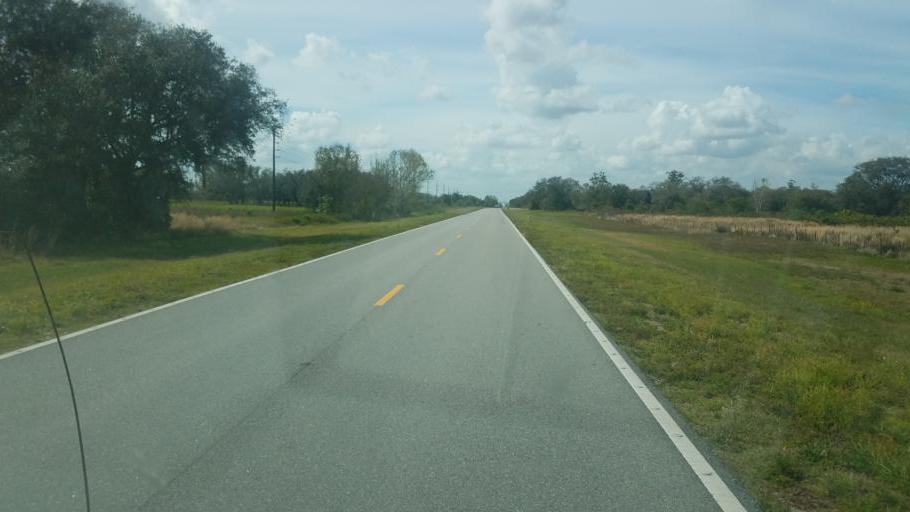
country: US
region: Florida
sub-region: Okeechobee County
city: Cypress Quarters
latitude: 27.4493
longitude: -80.7663
